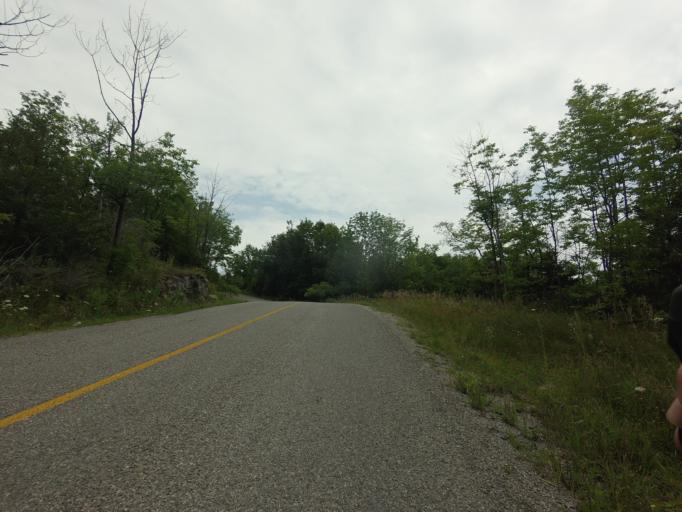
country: CA
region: Ontario
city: Kingston
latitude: 44.6079
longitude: -76.6424
